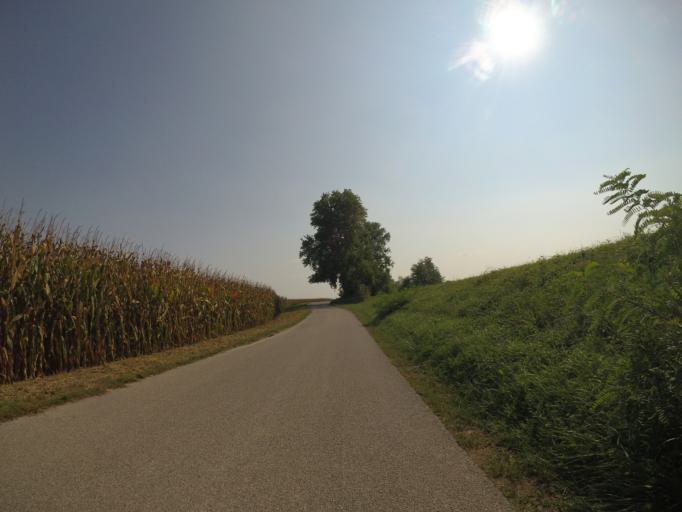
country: IT
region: Friuli Venezia Giulia
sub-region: Provincia di Udine
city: Camino al Tagliamento
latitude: 45.9464
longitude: 12.9168
